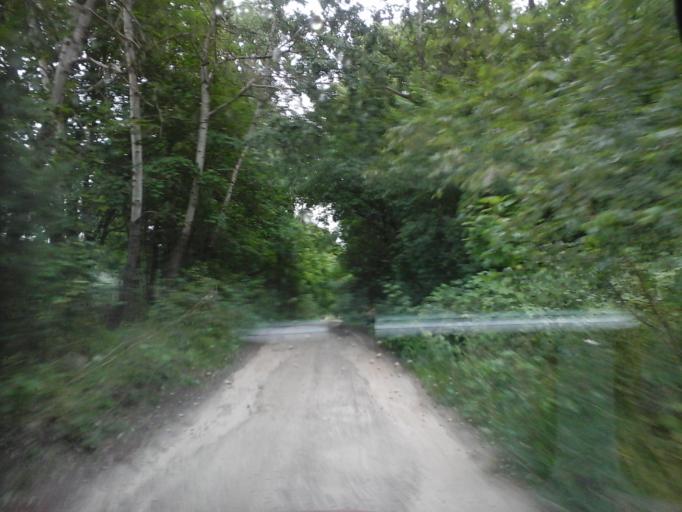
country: PL
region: West Pomeranian Voivodeship
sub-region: Powiat choszczenski
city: Bierzwnik
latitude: 53.1038
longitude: 15.6334
